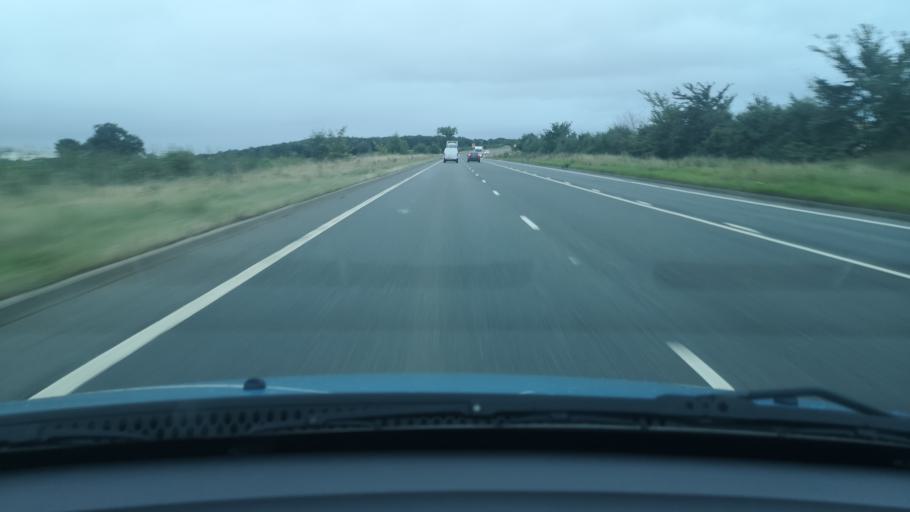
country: GB
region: England
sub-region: City and Borough of Wakefield
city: North Elmsall
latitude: 53.6171
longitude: -1.2431
